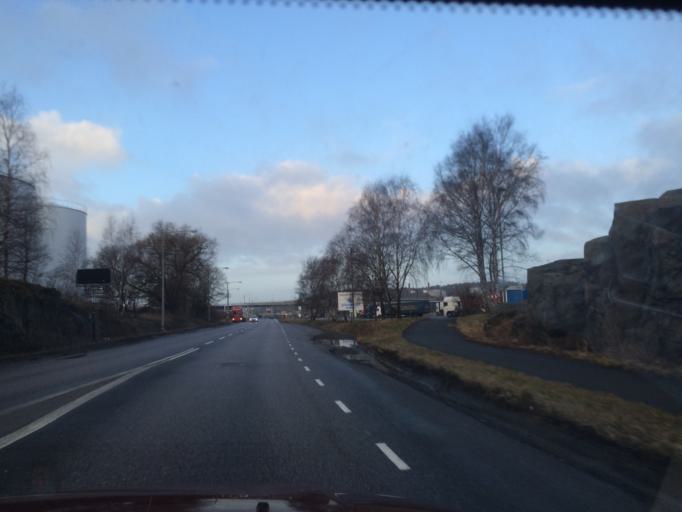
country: SE
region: Vaestra Goetaland
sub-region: Goteborg
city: Majorna
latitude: 57.6989
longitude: 11.8670
